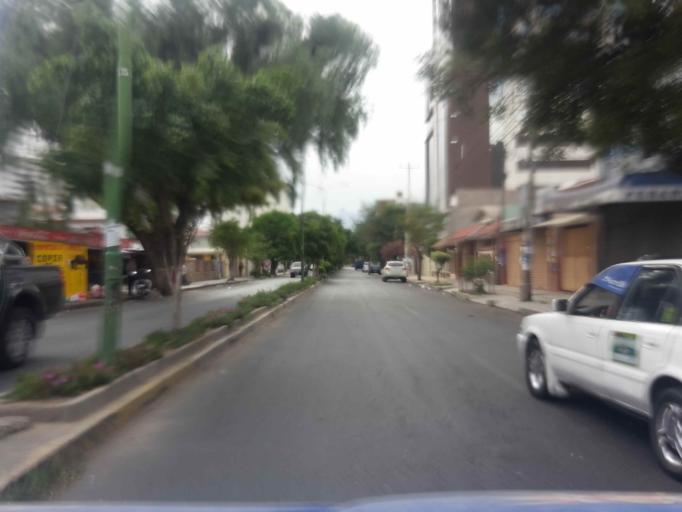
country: BO
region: Cochabamba
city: Cochabamba
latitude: -17.3838
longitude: -66.1473
